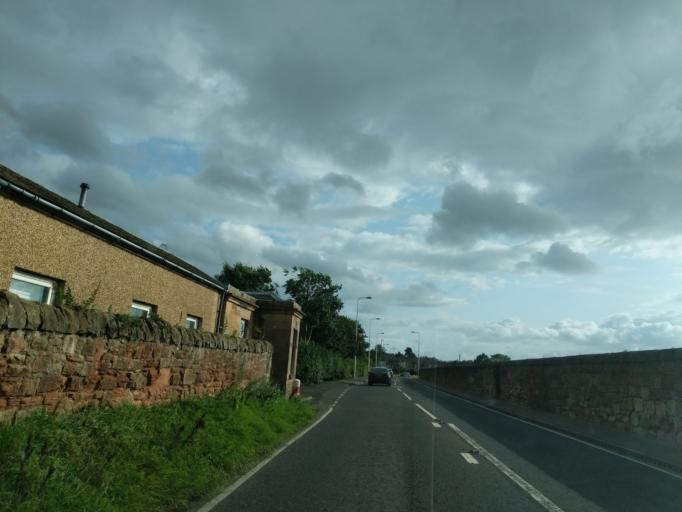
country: GB
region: Scotland
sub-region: Midlothian
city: Dalkeith
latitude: 55.8993
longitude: -3.0532
